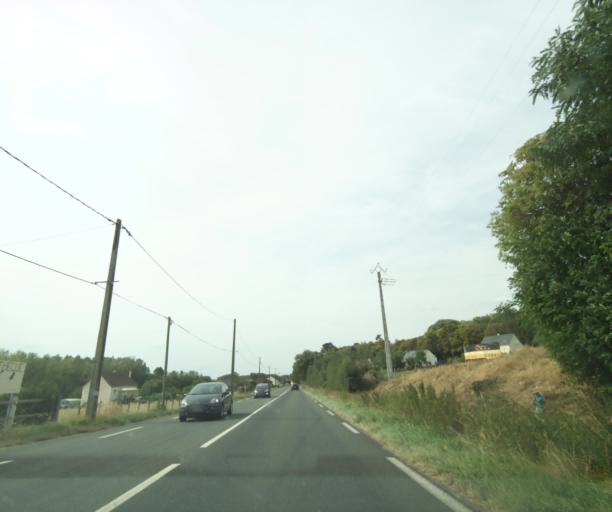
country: FR
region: Centre
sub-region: Departement d'Indre-et-Loire
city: Saint-Christophe-sur-le-Nais
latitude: 47.6599
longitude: 0.4774
